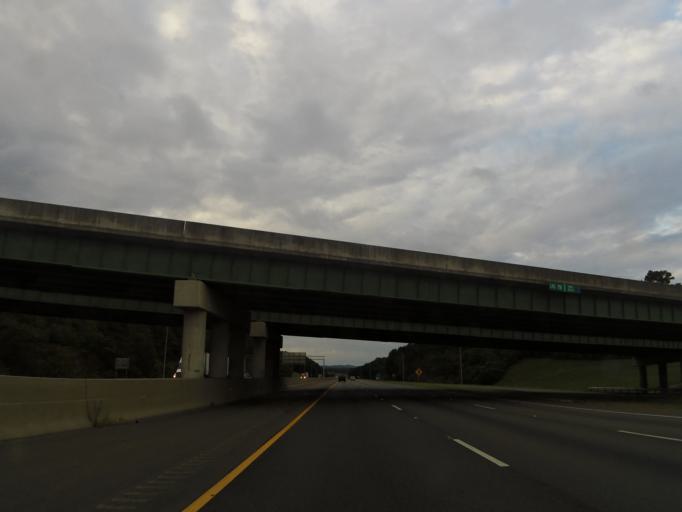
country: US
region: Alabama
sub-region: Jefferson County
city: Irondale
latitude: 33.5483
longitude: -86.6422
